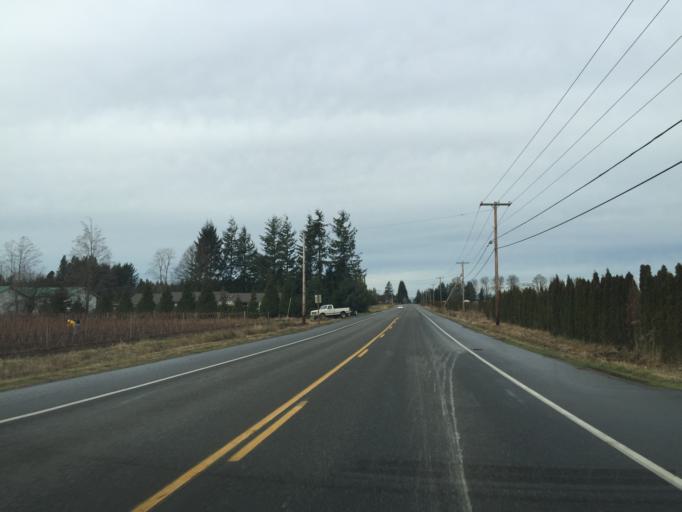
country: US
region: Washington
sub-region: Whatcom County
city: Ferndale
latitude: 48.8624
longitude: -122.5409
